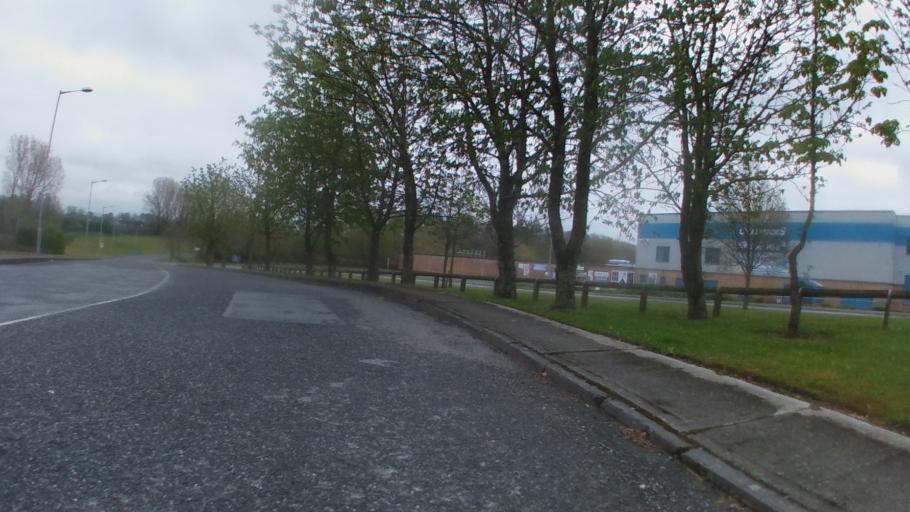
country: IE
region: Leinster
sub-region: Kilkenny
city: Kilkenny
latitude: 52.6475
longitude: -7.2202
